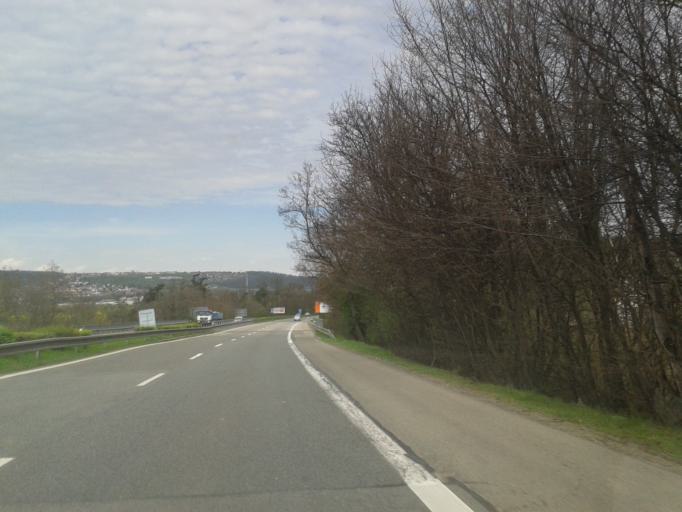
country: CZ
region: Central Bohemia
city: Vrane nad Vltavou
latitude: 49.9680
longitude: 14.3762
